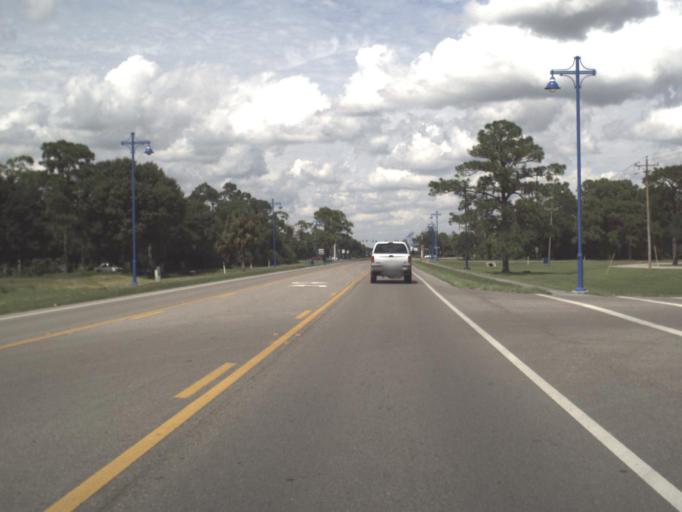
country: US
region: Florida
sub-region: Collier County
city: Immokalee
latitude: 26.4383
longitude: -81.4339
